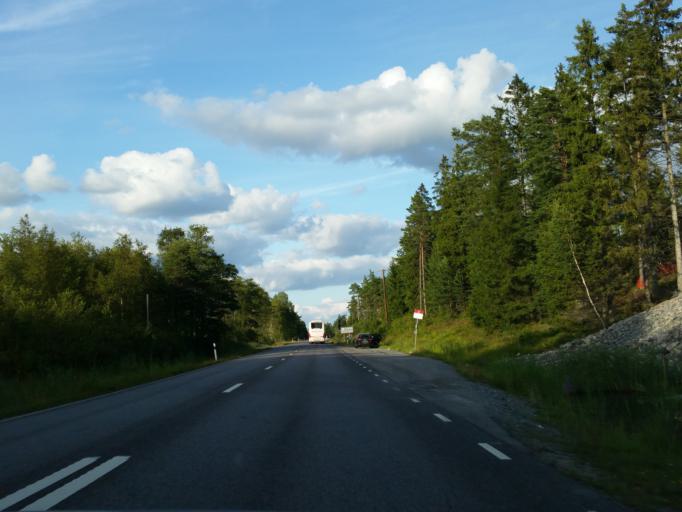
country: SE
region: Stockholm
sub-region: Sodertalje Kommun
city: Molnbo
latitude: 59.0668
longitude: 17.5259
